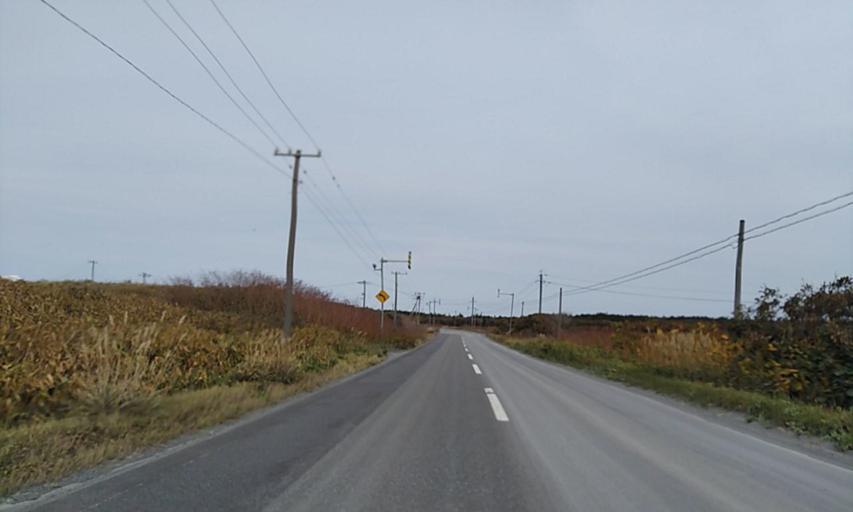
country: JP
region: Hokkaido
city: Makubetsu
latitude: 44.9947
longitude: 141.6895
